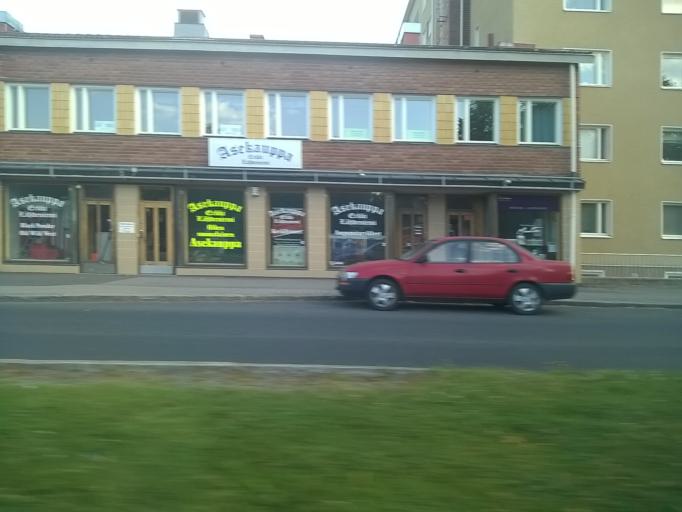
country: FI
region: Pirkanmaa
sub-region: Tampere
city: Tampere
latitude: 61.5016
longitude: 23.8012
